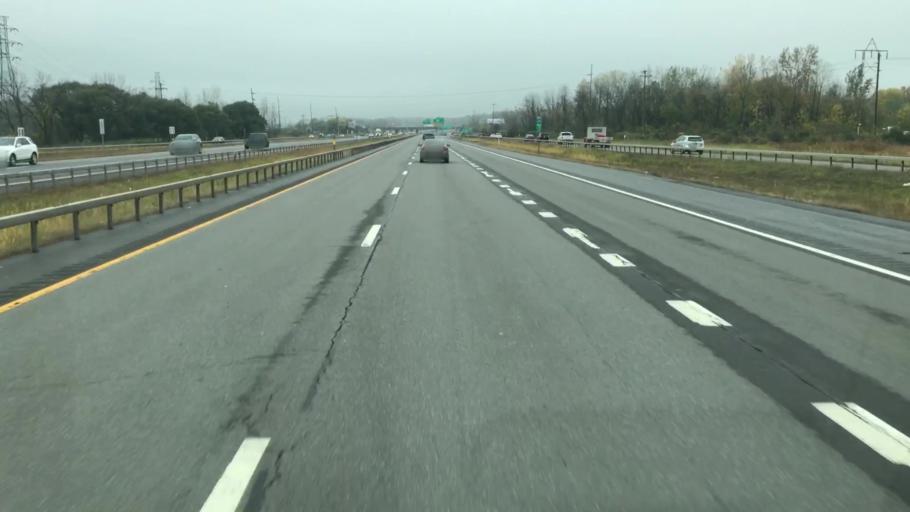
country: US
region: New York
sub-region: Onondaga County
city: East Syracuse
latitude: 43.0576
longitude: -76.0714
